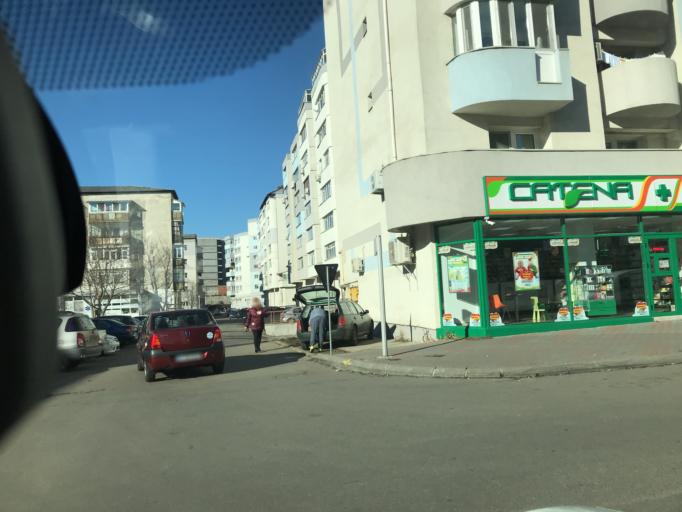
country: RO
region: Olt
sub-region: Municipiul Slatina
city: Slatina
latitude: 44.4249
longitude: 24.3771
